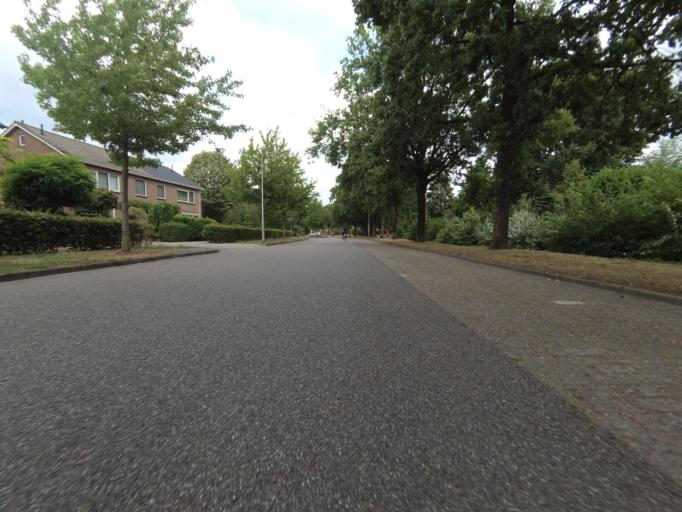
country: NL
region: Overijssel
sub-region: Gemeente Haaksbergen
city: Haaksbergen
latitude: 52.1626
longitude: 6.7428
